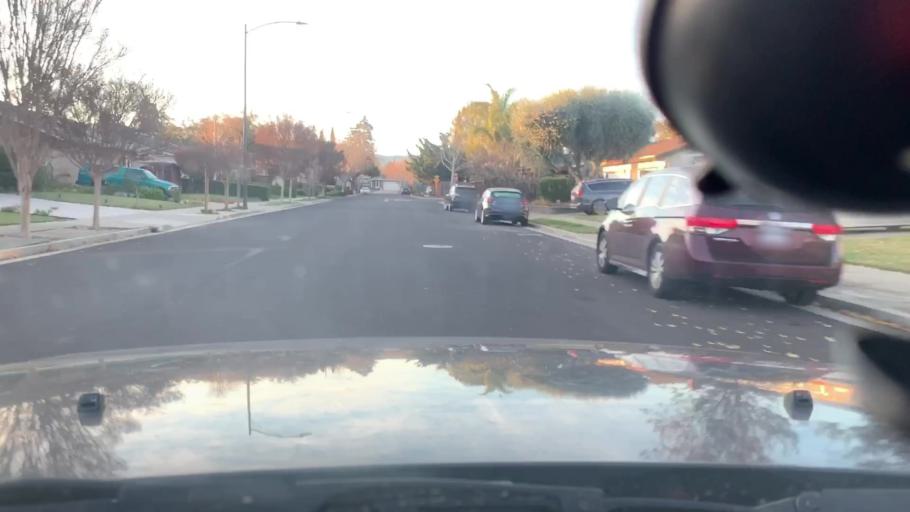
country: US
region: California
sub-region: Santa Clara County
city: Campbell
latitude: 37.2891
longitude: -121.9630
